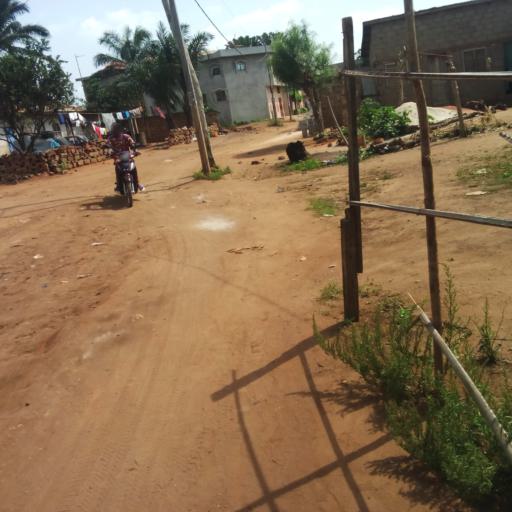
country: BJ
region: Atlantique
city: Abomey-Calavi
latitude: 6.4260
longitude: 2.3173
